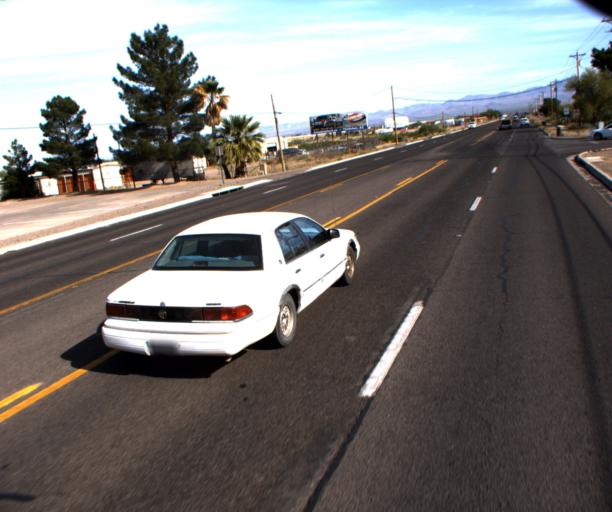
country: US
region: Arizona
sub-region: Graham County
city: Cactus Flat
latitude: 32.7947
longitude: -109.7077
